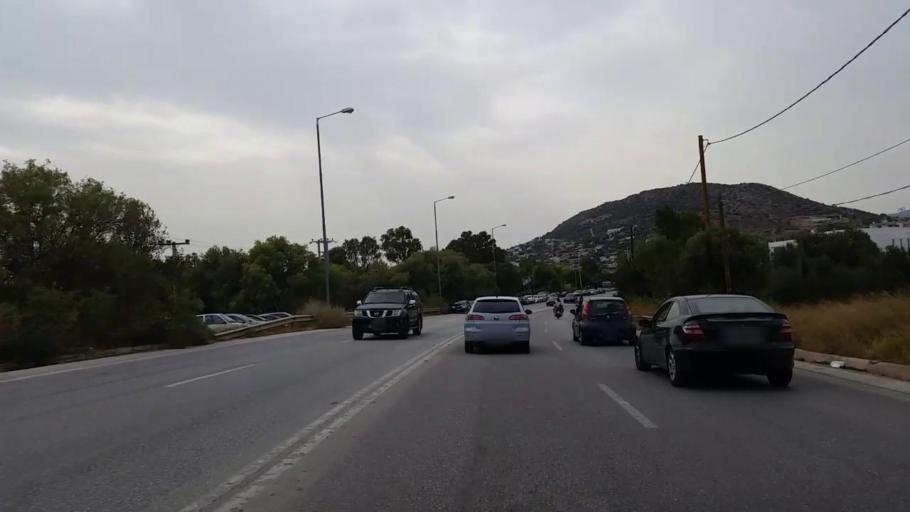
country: GR
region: Attica
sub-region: Nomarchia Anatolikis Attikis
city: Agios Dimitrios Kropias
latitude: 37.7953
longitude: 23.8733
